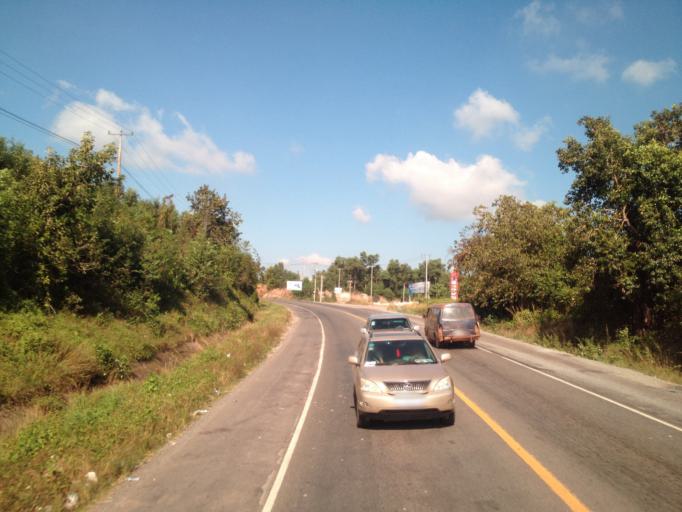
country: KH
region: Preah Sihanouk
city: Sihanoukville
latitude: 10.6049
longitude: 103.6203
